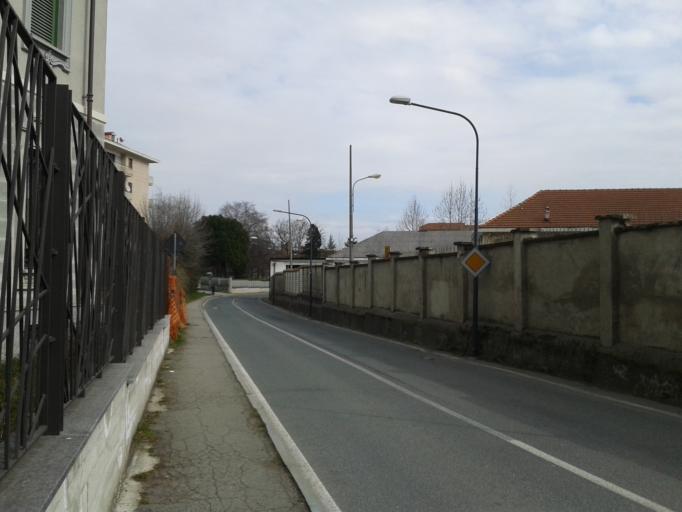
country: IT
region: Piedmont
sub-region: Provincia di Torino
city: Pinerolo
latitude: 44.8903
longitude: 7.3355
